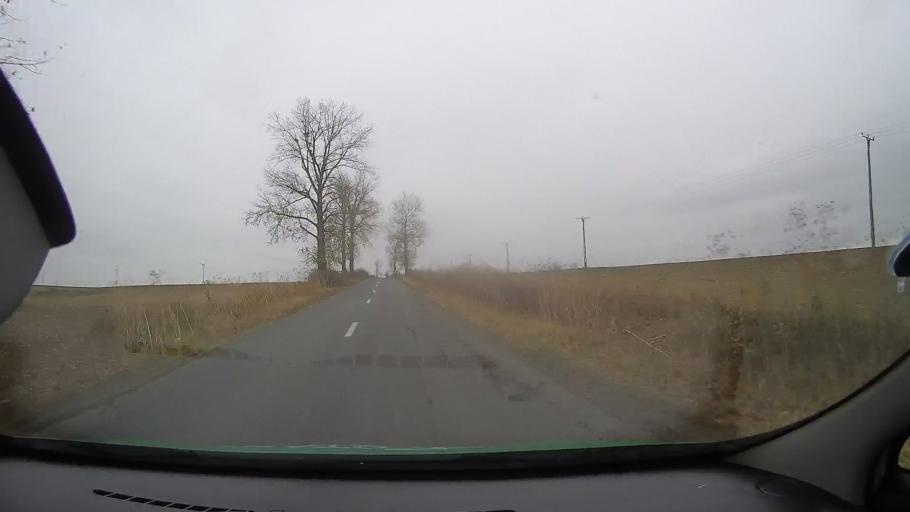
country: RO
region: Constanta
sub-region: Comuna Pantelimon
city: Pantelimon
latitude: 44.5591
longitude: 28.3228
